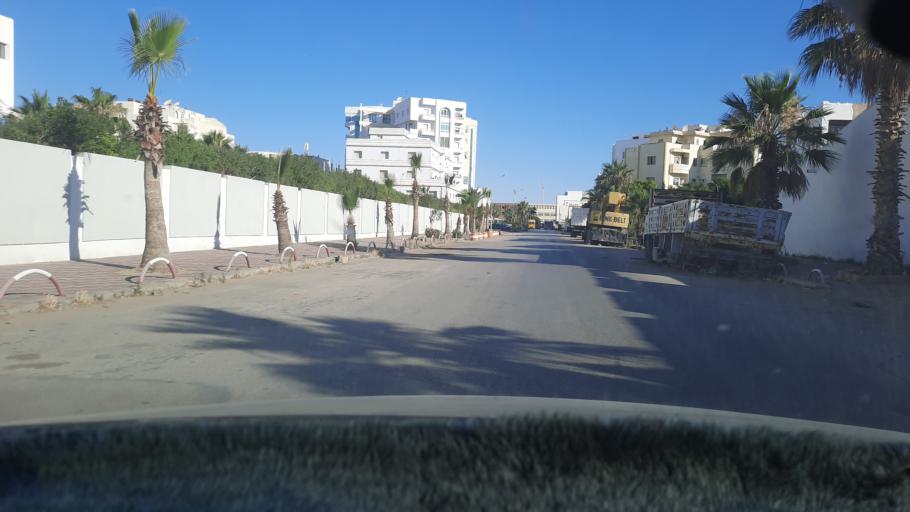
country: TN
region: Safaqis
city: Sfax
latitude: 34.7290
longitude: 10.7525
